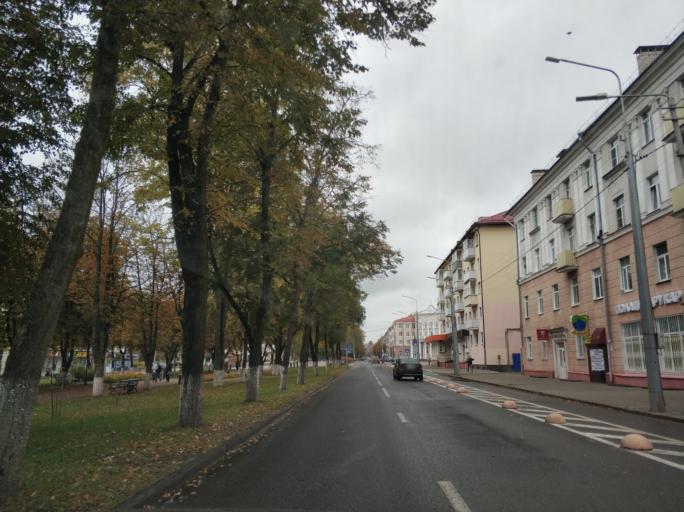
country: BY
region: Vitebsk
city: Polatsk
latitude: 55.4845
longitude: 28.7807
